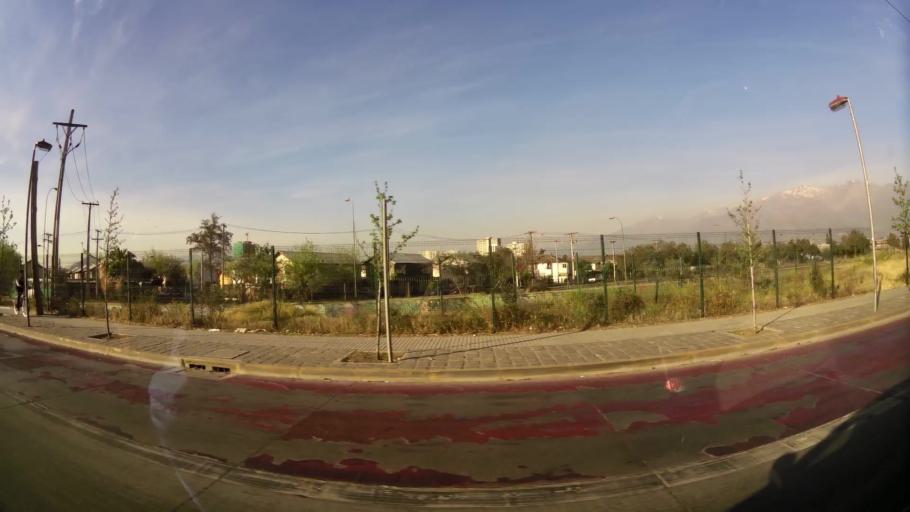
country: CL
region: Santiago Metropolitan
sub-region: Provincia de Santiago
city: Santiago
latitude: -33.4819
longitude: -70.6296
